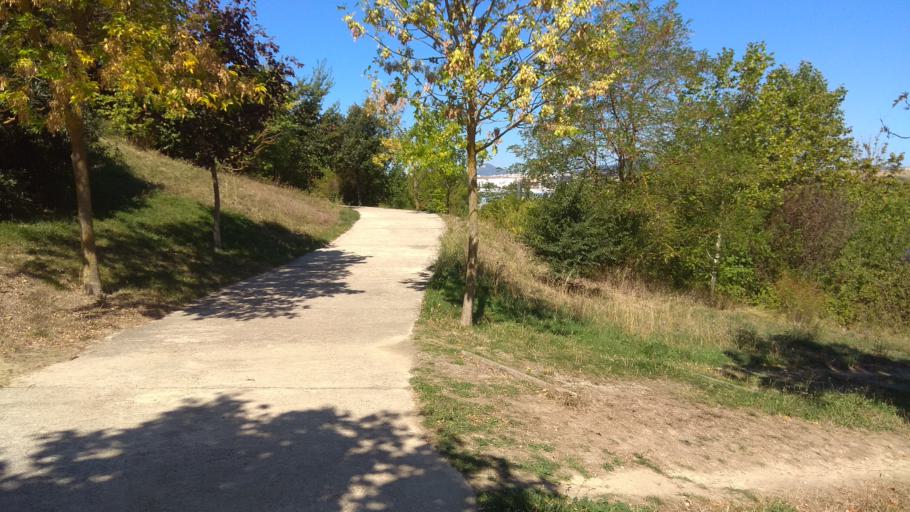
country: ES
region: Navarre
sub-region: Provincia de Navarra
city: Baranain
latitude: 42.8078
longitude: -1.6787
